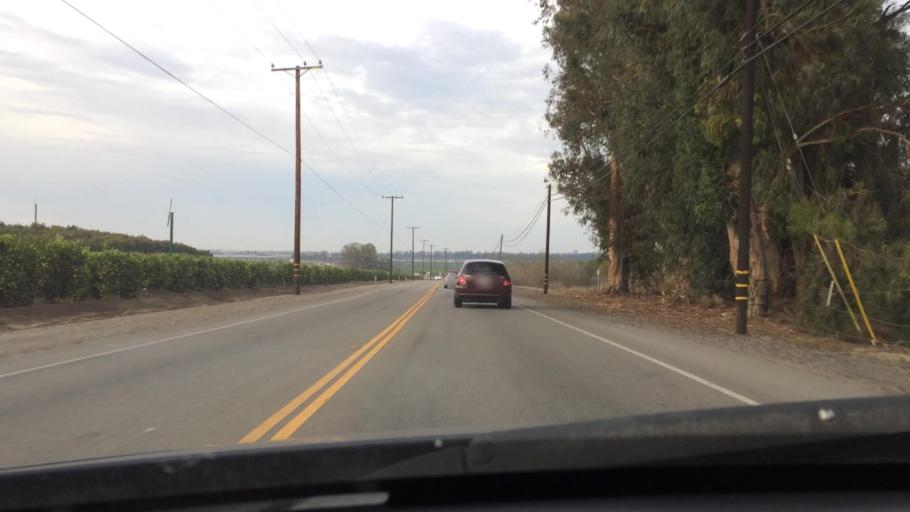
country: US
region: California
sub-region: Ventura County
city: Saticoy
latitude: 34.2611
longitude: -119.1023
